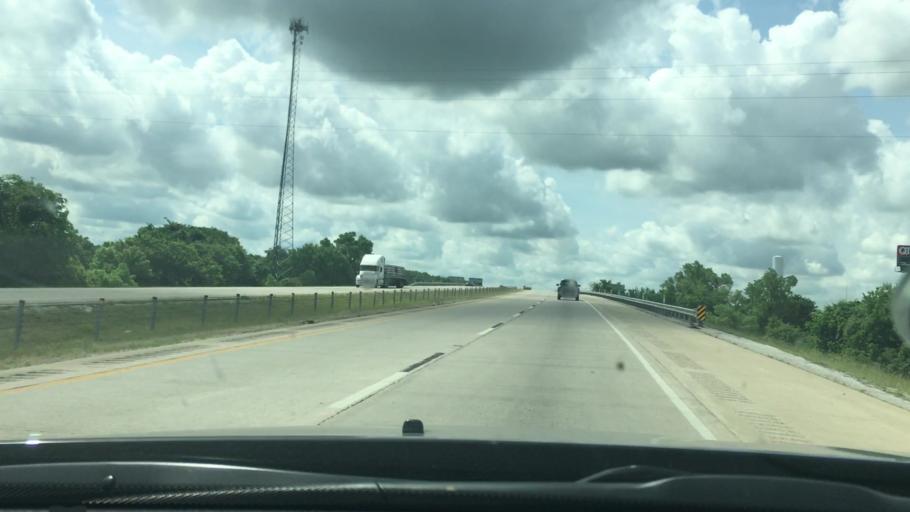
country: US
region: Oklahoma
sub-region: Love County
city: Marietta
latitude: 33.8391
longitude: -97.1331
